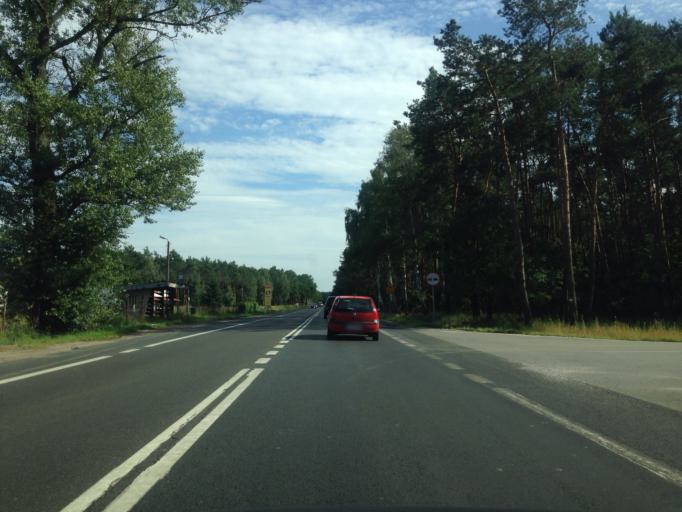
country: PL
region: Kujawsko-Pomorskie
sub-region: Powiat aleksandrowski
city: Aleksandrow Kujawski
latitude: 52.8948
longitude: 18.7292
